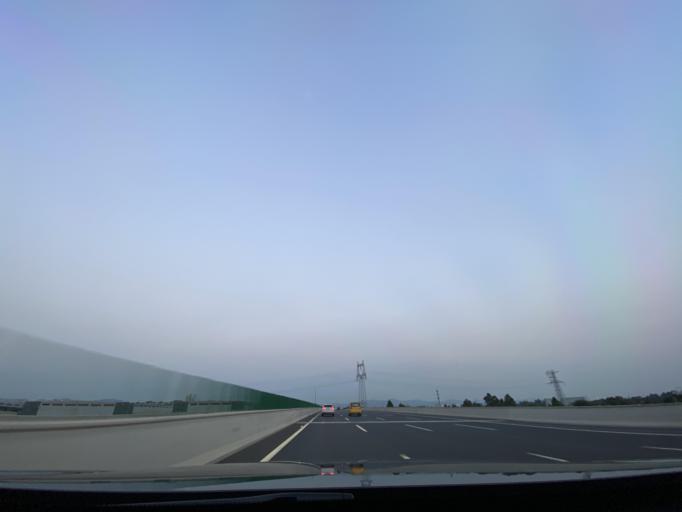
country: CN
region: Sichuan
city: Longquan
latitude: 30.5343
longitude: 104.1615
